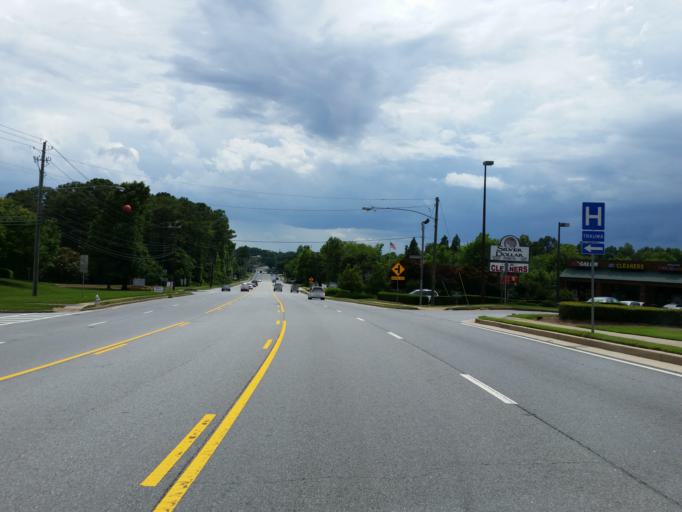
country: US
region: Georgia
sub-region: Fulton County
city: Alpharetta
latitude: 34.0643
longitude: -84.3217
